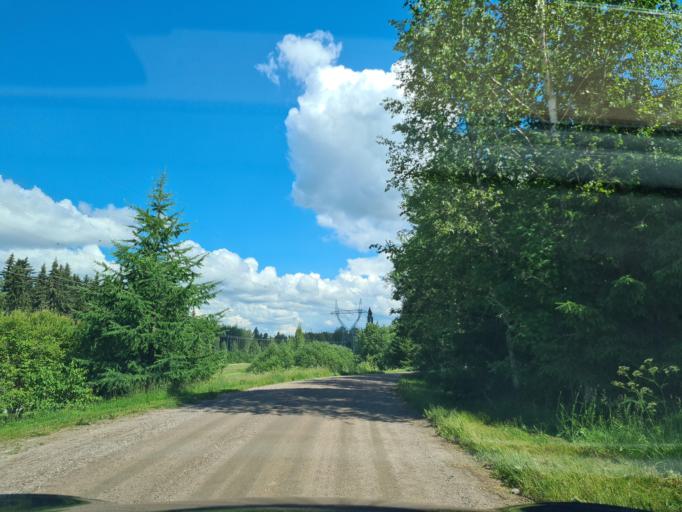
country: FI
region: Uusimaa
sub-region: Helsinki
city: Kaerkoelae
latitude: 60.7543
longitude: 23.9386
